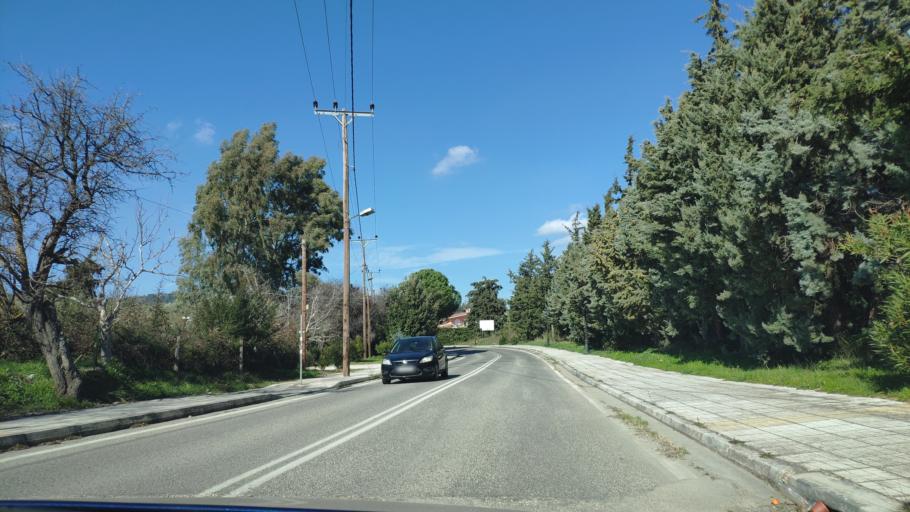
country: GR
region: Attica
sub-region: Nomarchia Anatolikis Attikis
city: Afidnes
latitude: 38.1943
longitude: 23.8432
